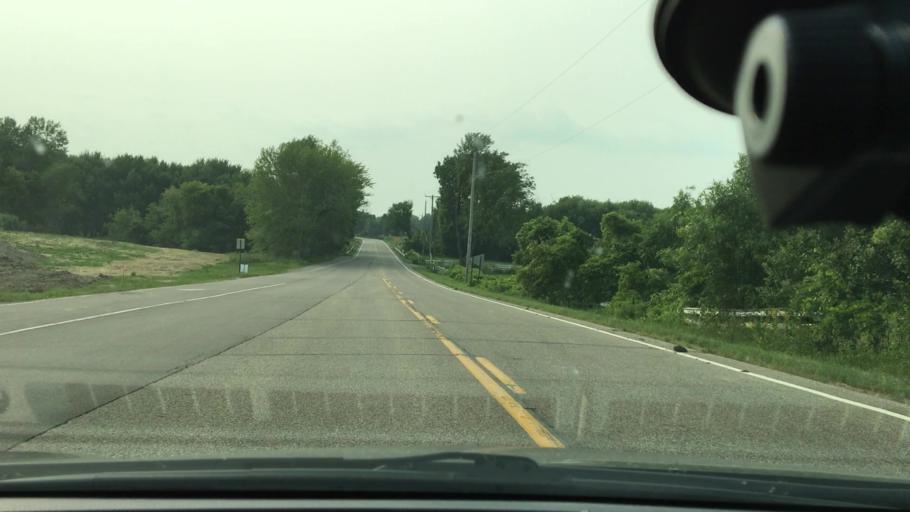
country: US
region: Minnesota
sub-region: Anoka County
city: Ramsey
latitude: 45.2219
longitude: -93.4645
